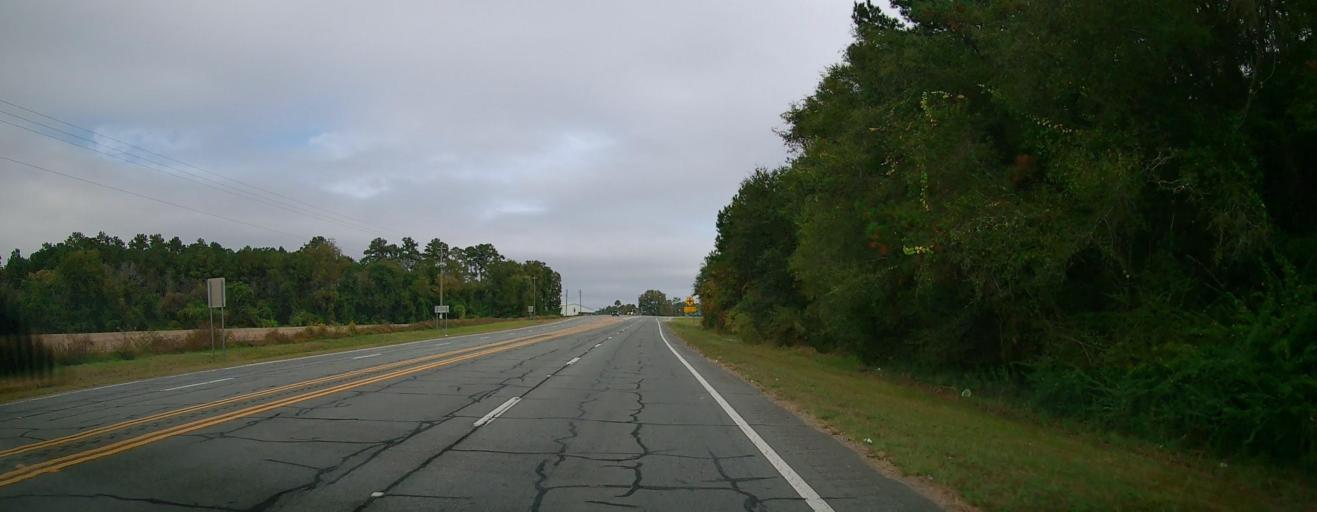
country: US
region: Georgia
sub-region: Tift County
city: Omega
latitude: 31.3277
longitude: -83.6176
